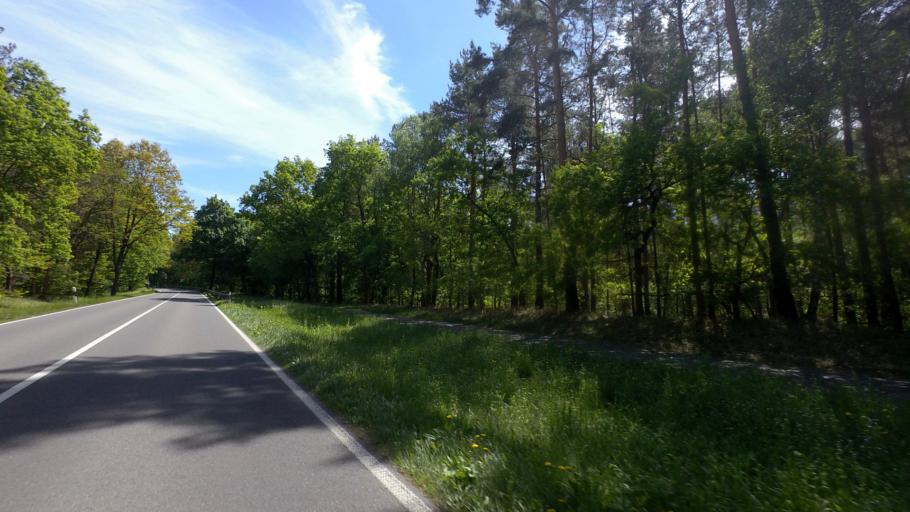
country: DE
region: Brandenburg
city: Luckenwalde
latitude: 52.0658
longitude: 13.2064
